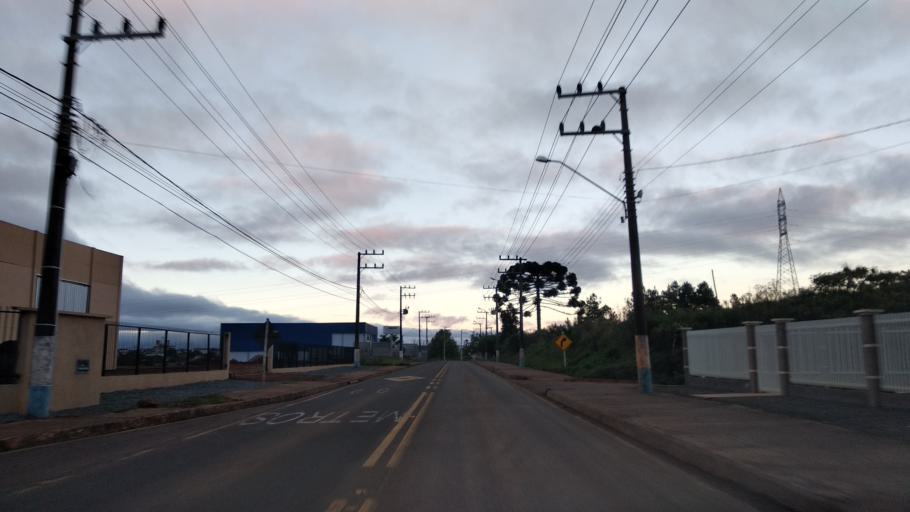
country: BR
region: Santa Catarina
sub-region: Campos Novos
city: Campos Novos
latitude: -27.3814
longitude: -51.2097
